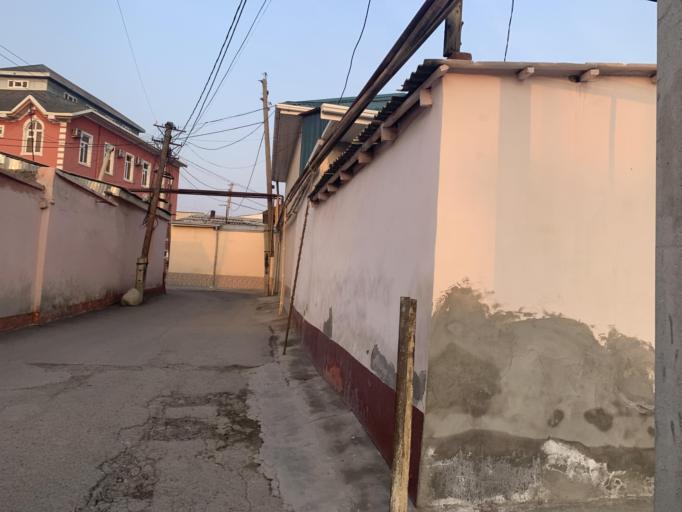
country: UZ
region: Fergana
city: Qo`qon
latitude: 40.5359
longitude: 70.9330
